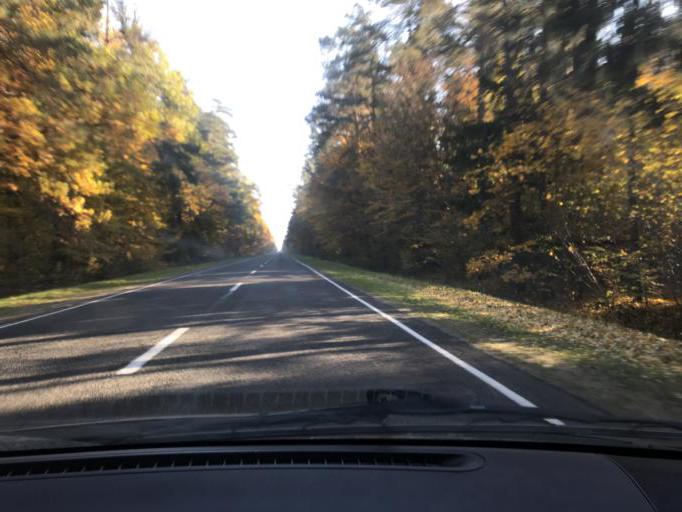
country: BY
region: Brest
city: Lyakhavichy
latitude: 52.9497
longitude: 26.1495
